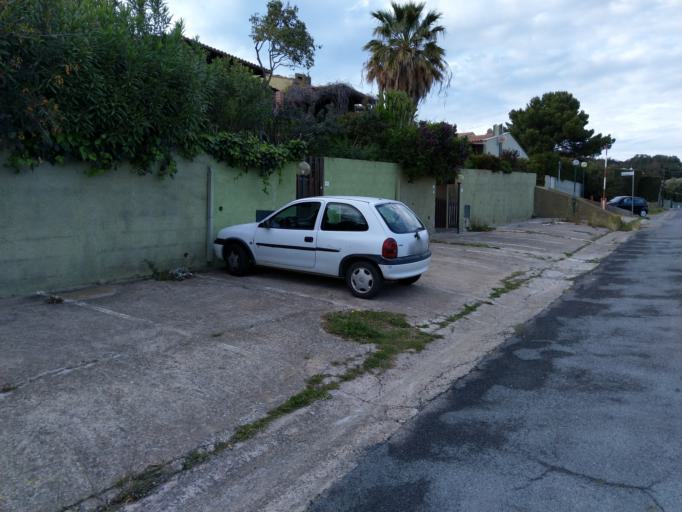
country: IT
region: Sardinia
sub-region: Provincia di Cagliari
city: Olia Speciosa
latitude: 39.2534
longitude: 9.5696
